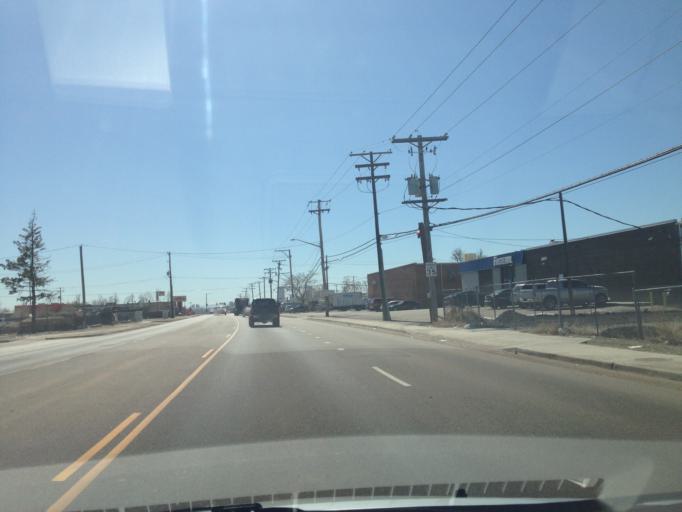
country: US
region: Colorado
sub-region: Adams County
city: Twin Lakes
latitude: 39.7997
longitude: -104.9782
